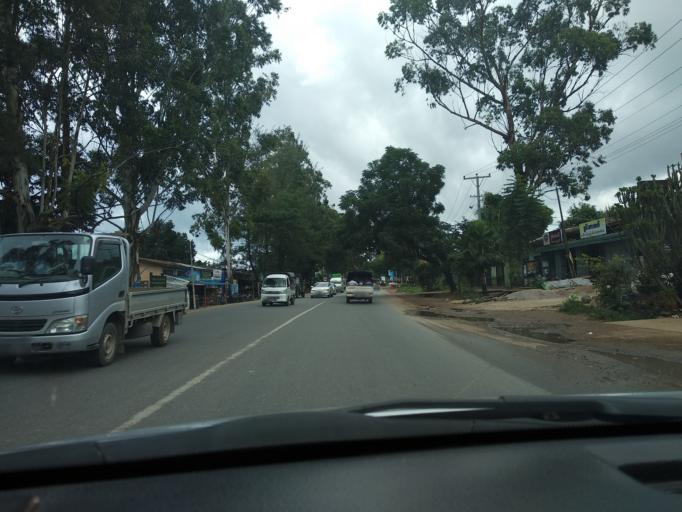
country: MM
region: Mandalay
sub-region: Pyin Oo Lwin District
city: Pyin Oo Lwin
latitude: 21.9775
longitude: 96.4078
